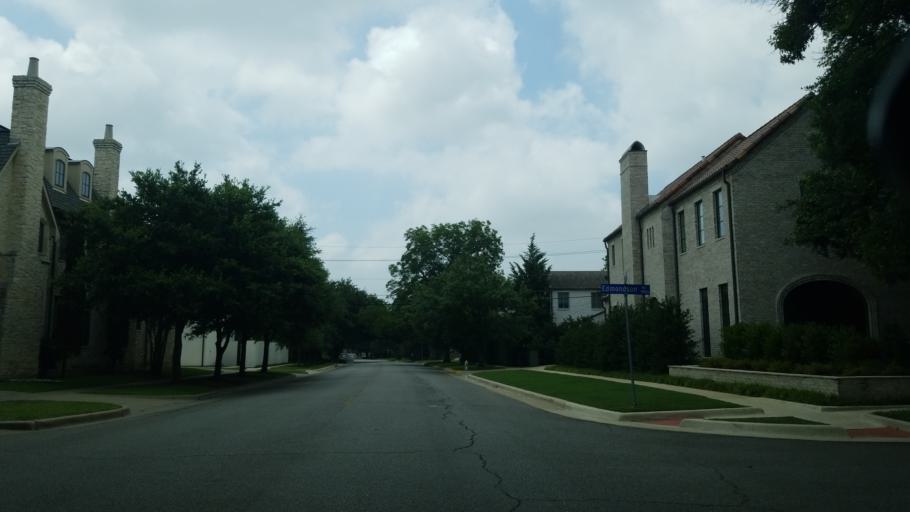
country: US
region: Texas
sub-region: Dallas County
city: Highland Park
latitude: 32.8340
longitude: -96.8104
